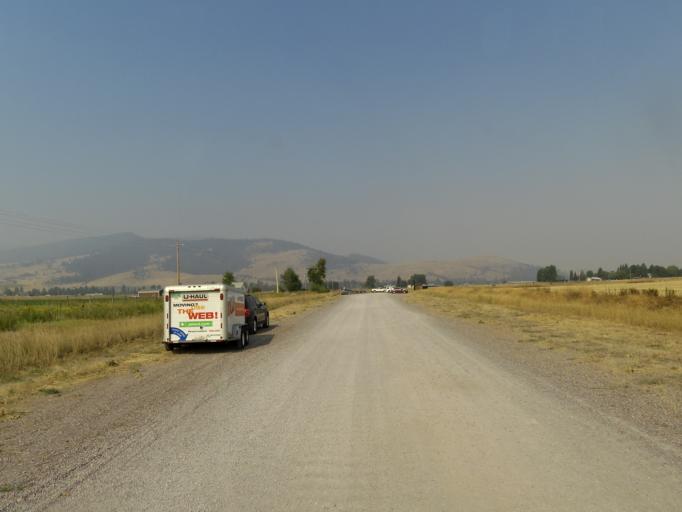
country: US
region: Montana
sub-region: Missoula County
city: Frenchtown
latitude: 47.1892
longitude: -114.0891
